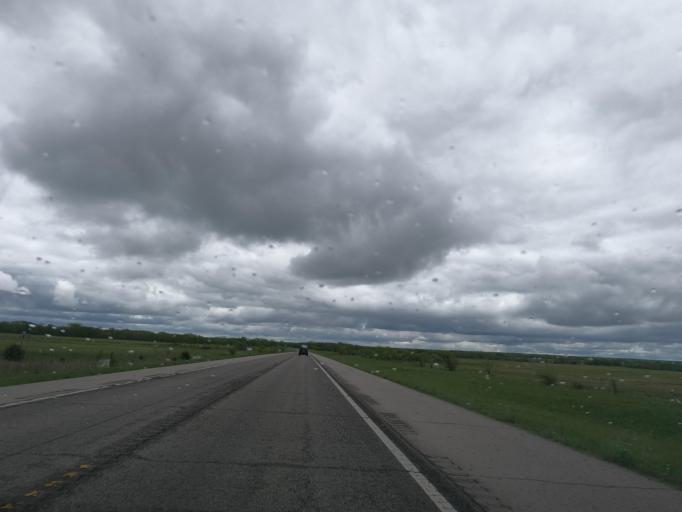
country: US
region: Kansas
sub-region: Montgomery County
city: Cherryvale
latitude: 37.3454
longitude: -95.4652
